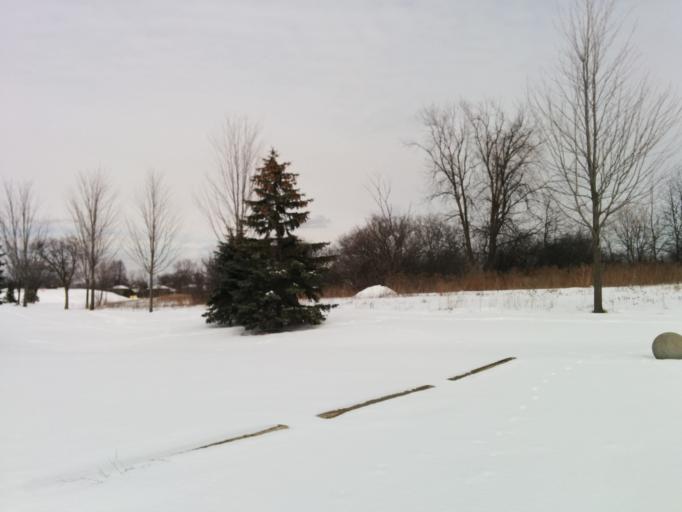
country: CA
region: Ontario
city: Mississauga
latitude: 43.5246
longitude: -79.6600
